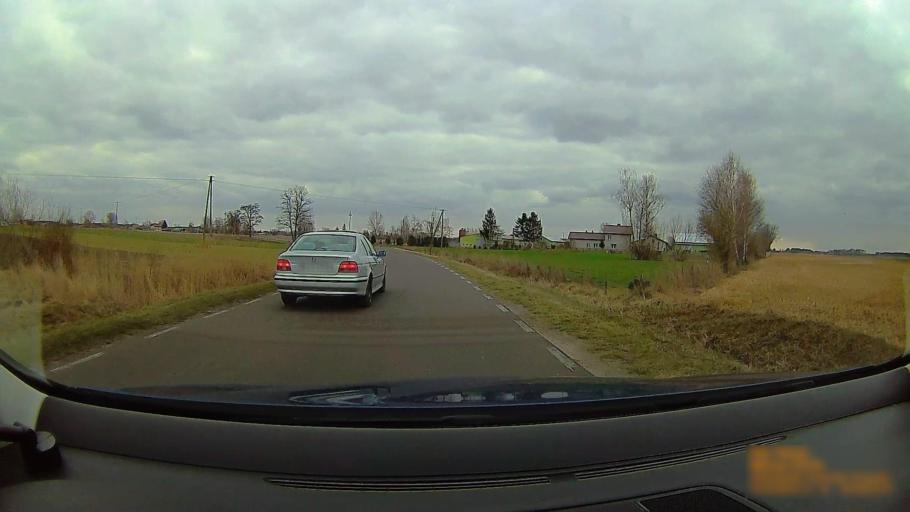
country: PL
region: Greater Poland Voivodeship
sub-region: Powiat koninski
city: Rzgow Pierwszy
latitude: 52.1141
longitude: 18.0725
